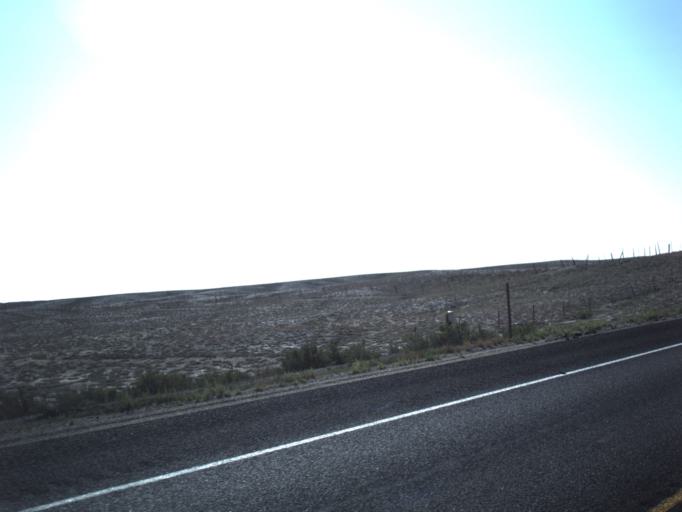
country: US
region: Utah
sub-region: Emery County
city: Ferron
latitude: 39.0517
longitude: -111.1231
